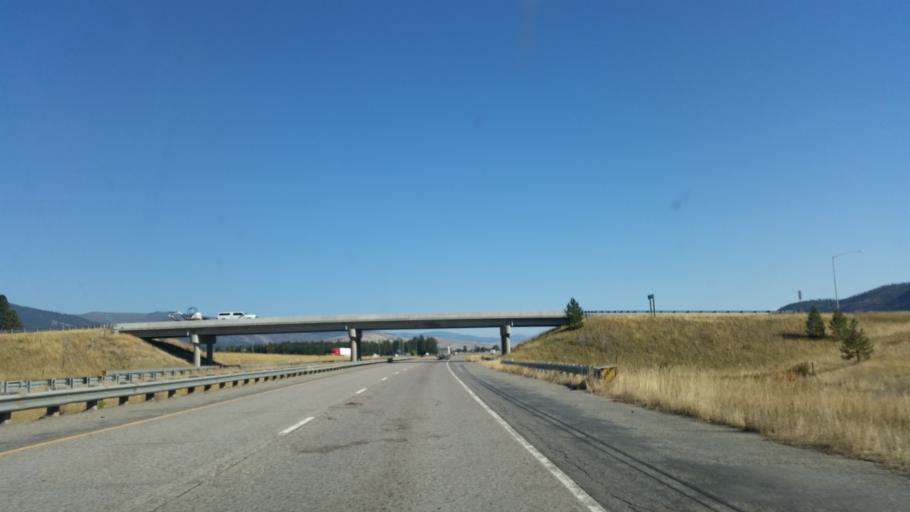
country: US
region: Montana
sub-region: Missoula County
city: Frenchtown
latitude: 47.0331
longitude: -114.3251
